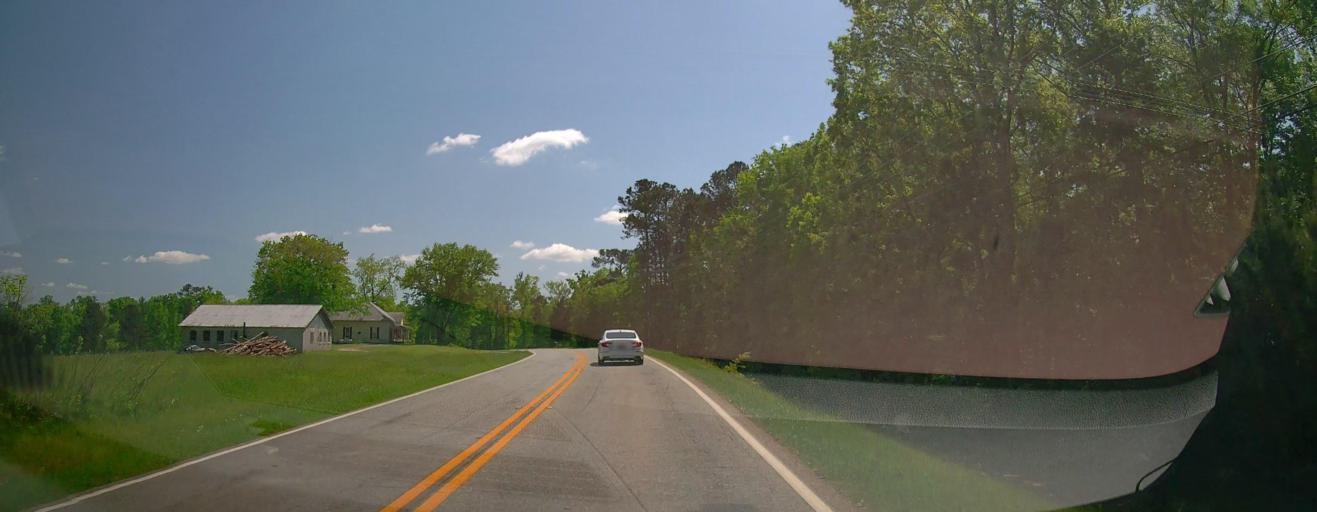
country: US
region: Georgia
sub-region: Putnam County
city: Eatonton
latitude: 33.2835
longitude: -83.3037
